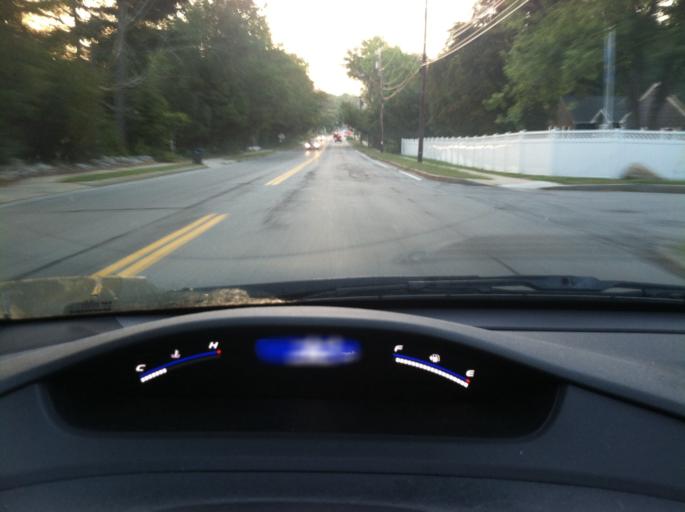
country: US
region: Massachusetts
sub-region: Middlesex County
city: Bedford
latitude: 42.4879
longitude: -71.2670
